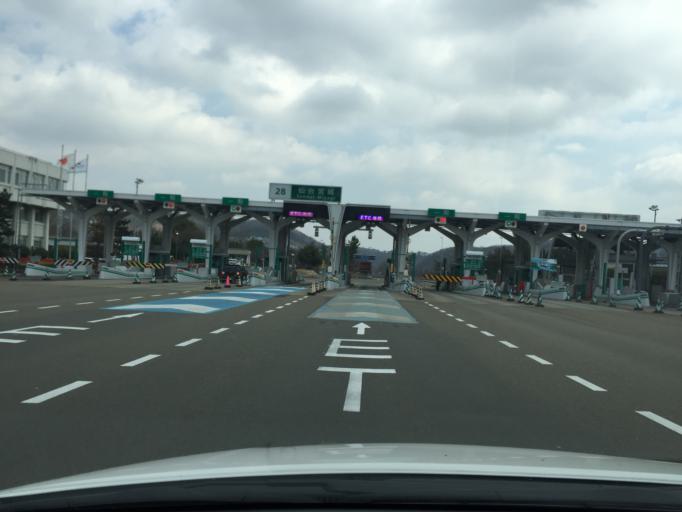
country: JP
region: Miyagi
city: Sendai
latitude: 38.2587
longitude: 140.8128
